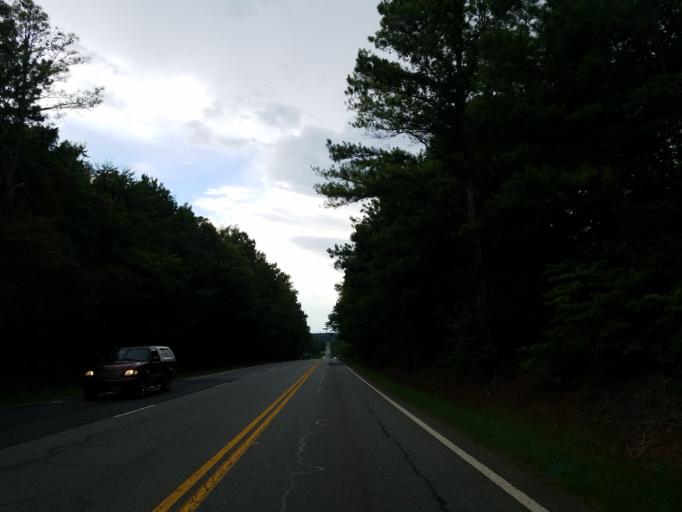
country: US
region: Georgia
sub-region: Bartow County
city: Adairsville
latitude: 34.3291
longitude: -84.9005
